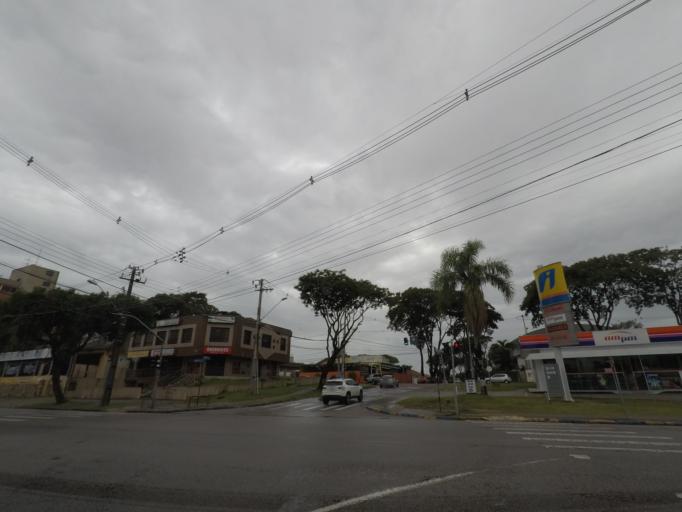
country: BR
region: Parana
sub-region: Curitiba
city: Curitiba
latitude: -25.4529
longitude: -49.2780
